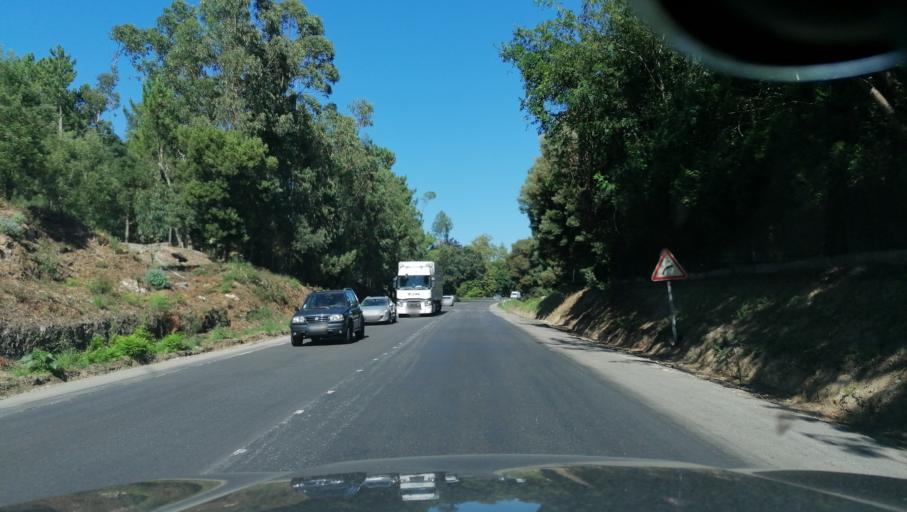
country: PT
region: Aveiro
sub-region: Santa Maria da Feira
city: Feira
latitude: 40.9321
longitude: -8.5467
